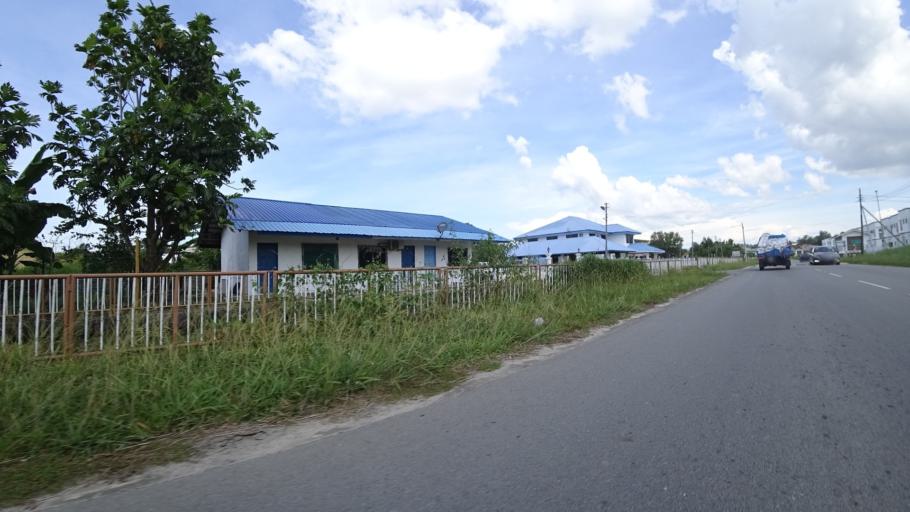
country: BN
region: Brunei and Muara
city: Bandar Seri Begawan
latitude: 4.8841
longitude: 114.8523
